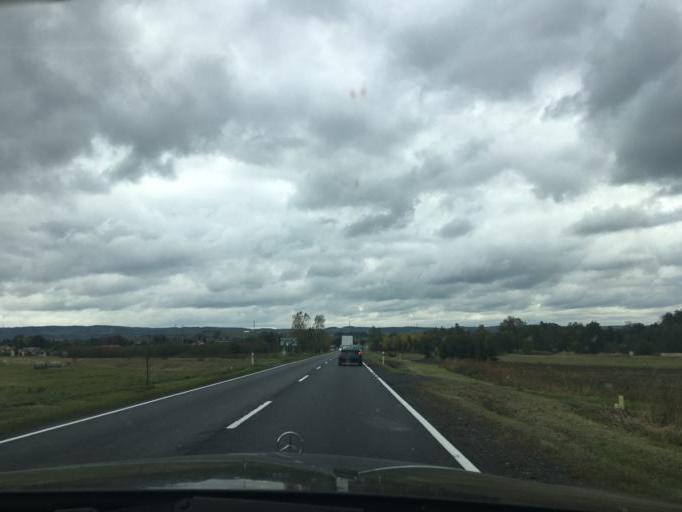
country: PL
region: Subcarpathian Voivodeship
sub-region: Powiat krosnienski
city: Kroscienko Wyzne
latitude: 49.6673
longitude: 21.8431
